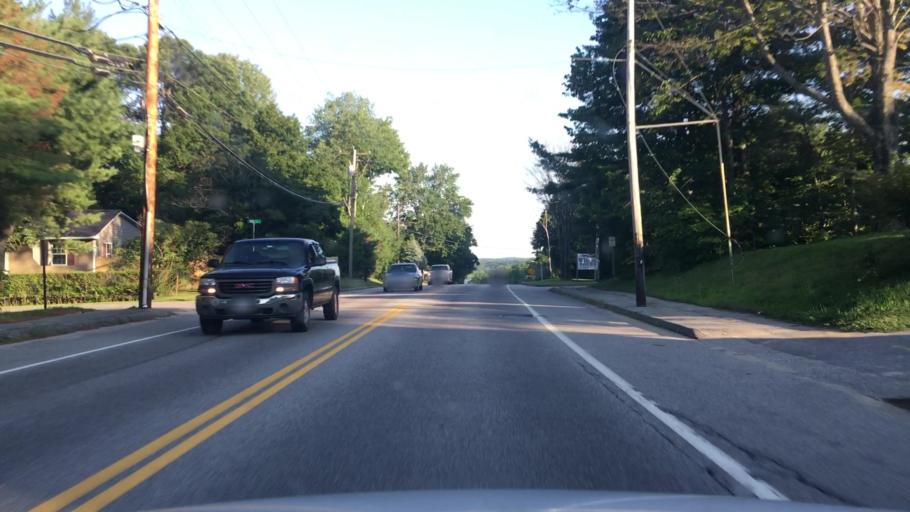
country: US
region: Maine
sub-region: Androscoggin County
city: Lisbon
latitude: 44.0169
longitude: -70.0914
